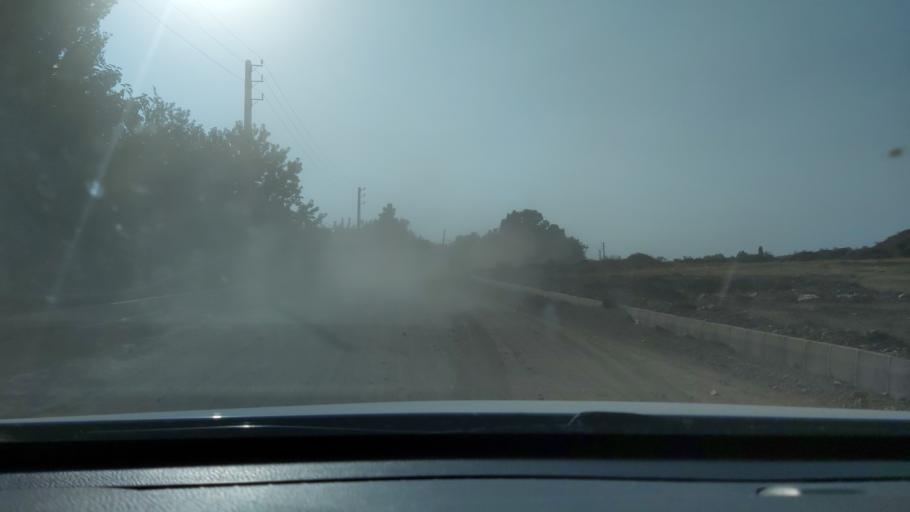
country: IR
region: Alborz
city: Hashtgerd
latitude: 35.9541
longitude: 50.7860
